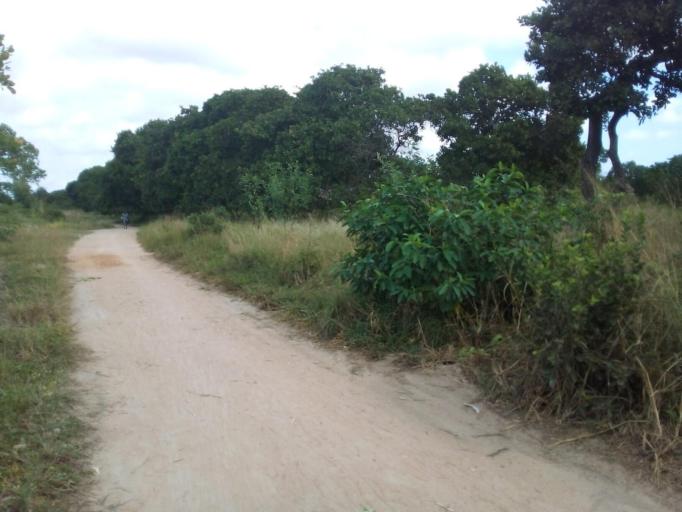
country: MZ
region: Zambezia
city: Quelimane
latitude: -17.5527
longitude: 36.7026
